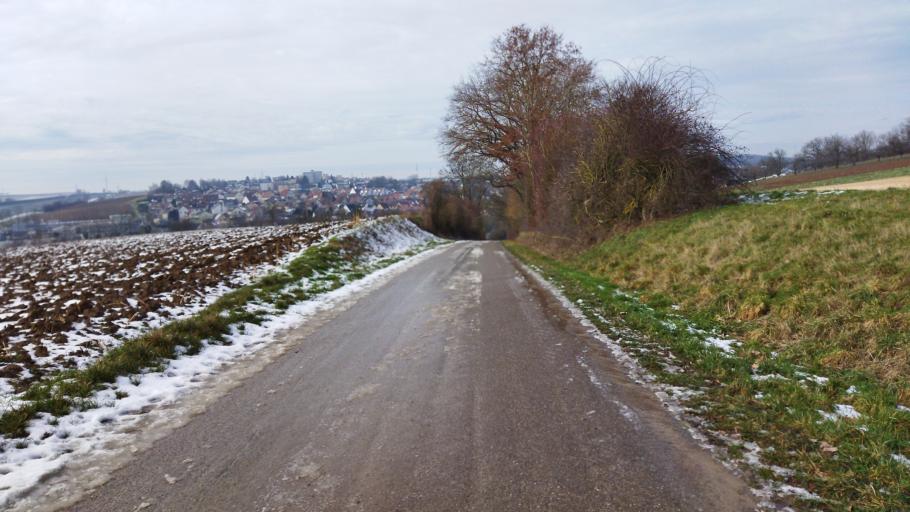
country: DE
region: Baden-Wuerttemberg
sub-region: Regierungsbezirk Stuttgart
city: Bad Wimpfen
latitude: 49.1918
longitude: 9.1555
